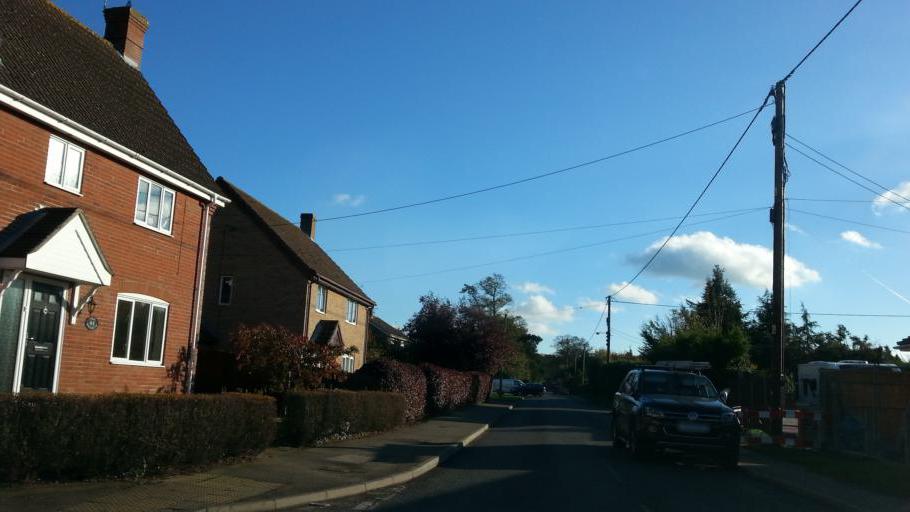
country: GB
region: England
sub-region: Suffolk
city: Thurston
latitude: 52.2535
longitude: 0.8055
